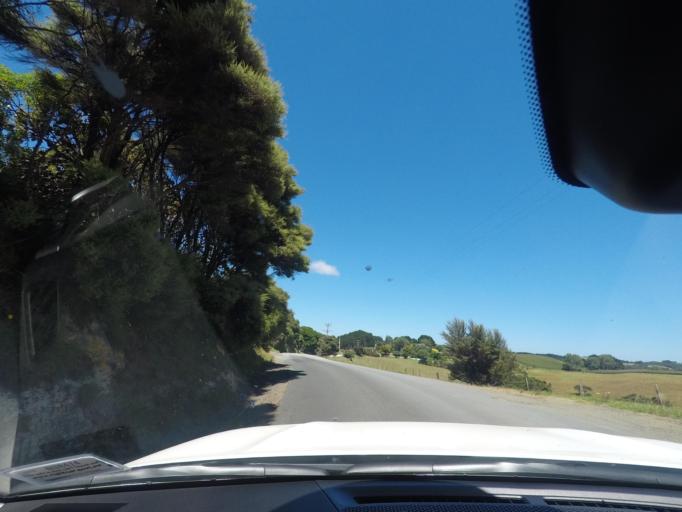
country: NZ
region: Auckland
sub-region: Auckland
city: Parakai
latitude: -36.5784
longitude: 174.3253
